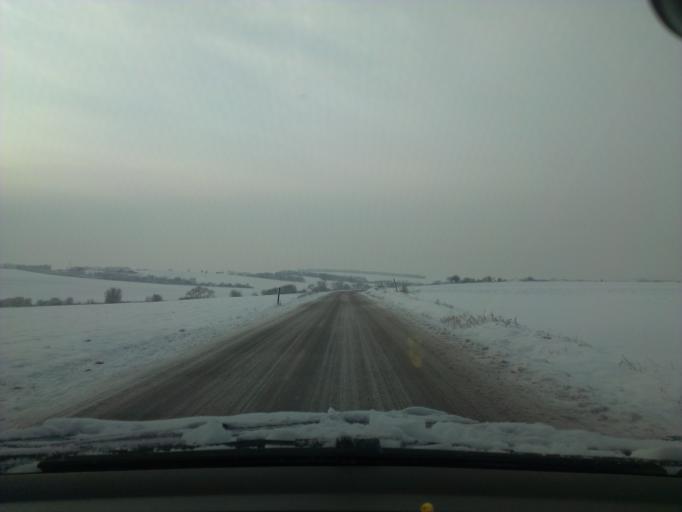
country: SK
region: Trnavsky
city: Hlohovec
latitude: 48.4879
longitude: 17.9887
